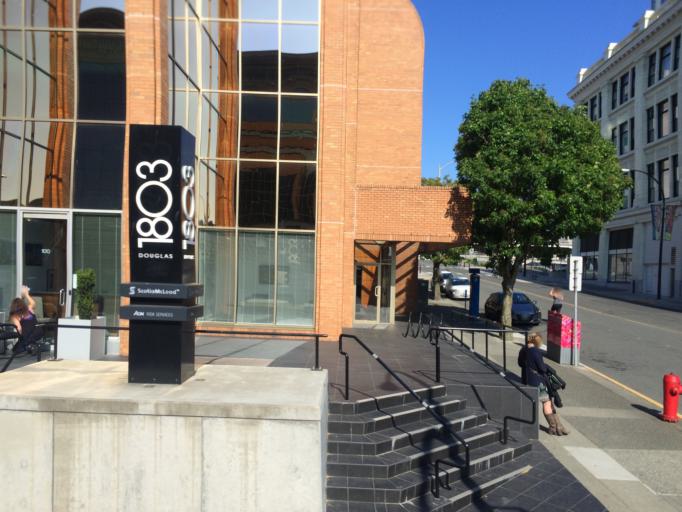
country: CA
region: British Columbia
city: Victoria
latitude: 48.4302
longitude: -123.3644
